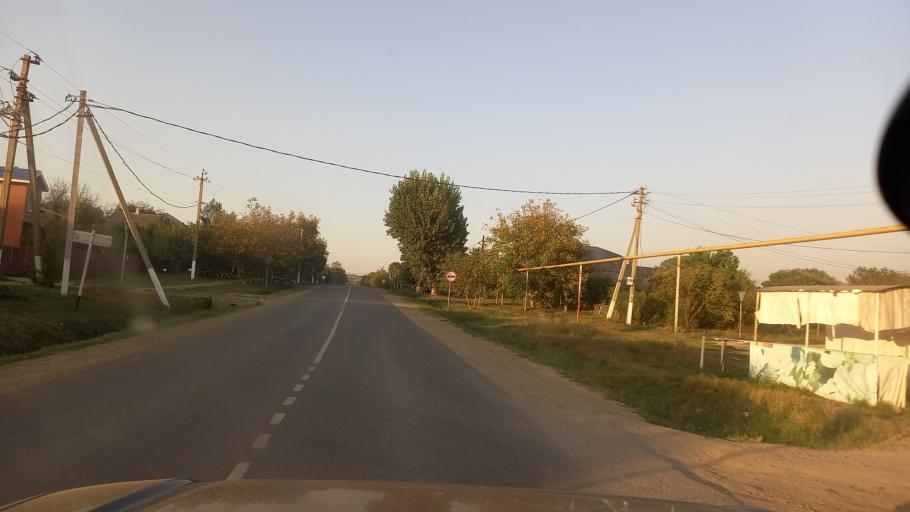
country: RU
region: Krasnodarskiy
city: Smolenskaya
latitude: 44.7696
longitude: 38.7823
